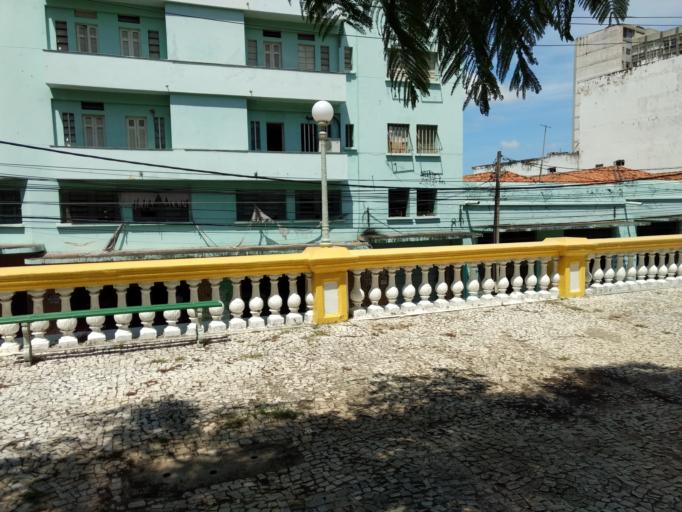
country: BR
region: Ceara
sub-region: Fortaleza
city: Fortaleza
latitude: -3.7267
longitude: -38.5260
